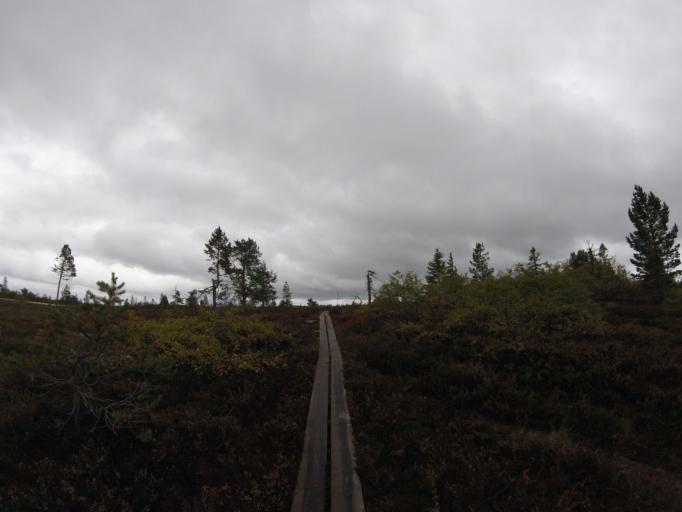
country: NO
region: Buskerud
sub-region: Flesberg
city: Lampeland
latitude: 59.7736
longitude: 9.4061
